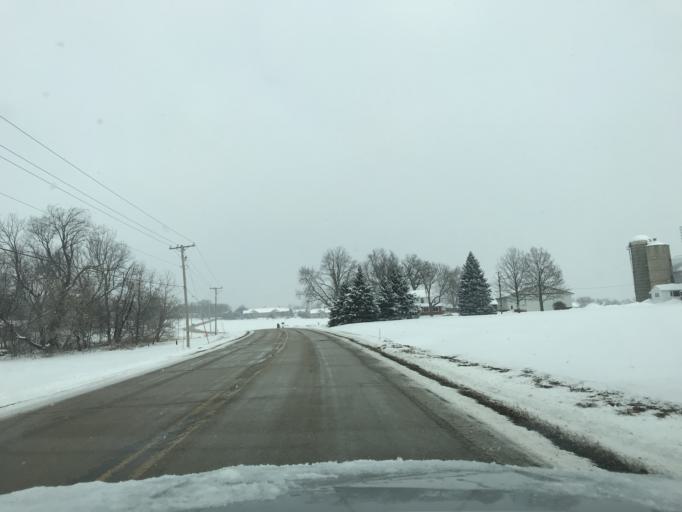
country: US
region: Wisconsin
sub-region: Dane County
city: Sun Prairie
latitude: 43.1706
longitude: -89.2855
